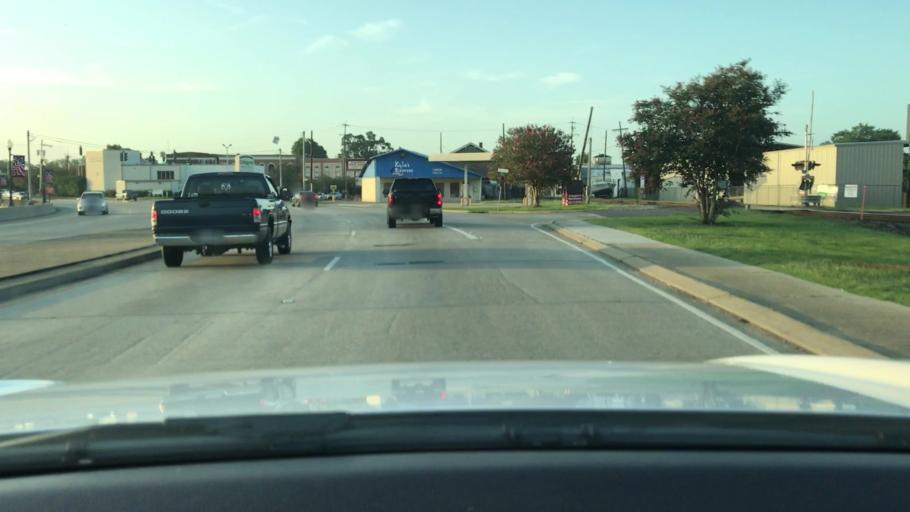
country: US
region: Louisiana
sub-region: Iberville Parish
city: Plaquemine
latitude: 30.2924
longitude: -91.2379
